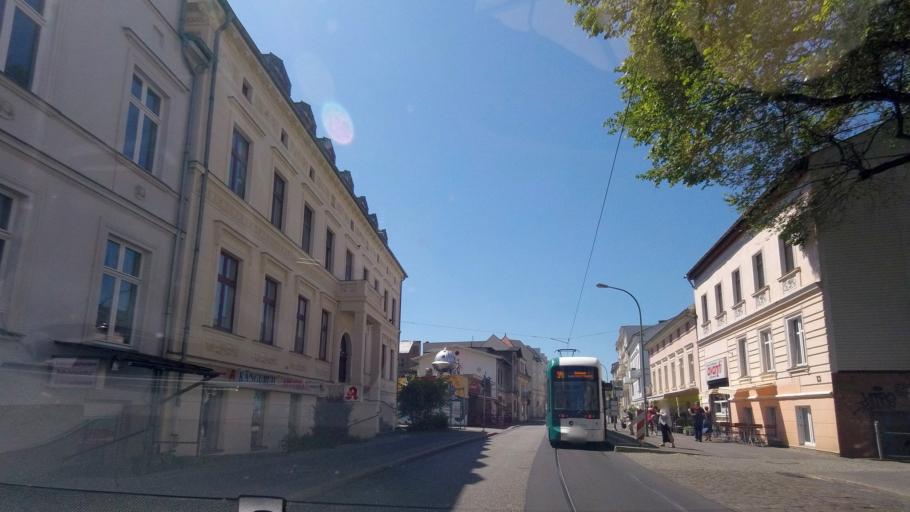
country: DE
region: Brandenburg
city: Potsdam
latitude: 52.3938
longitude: 13.0355
